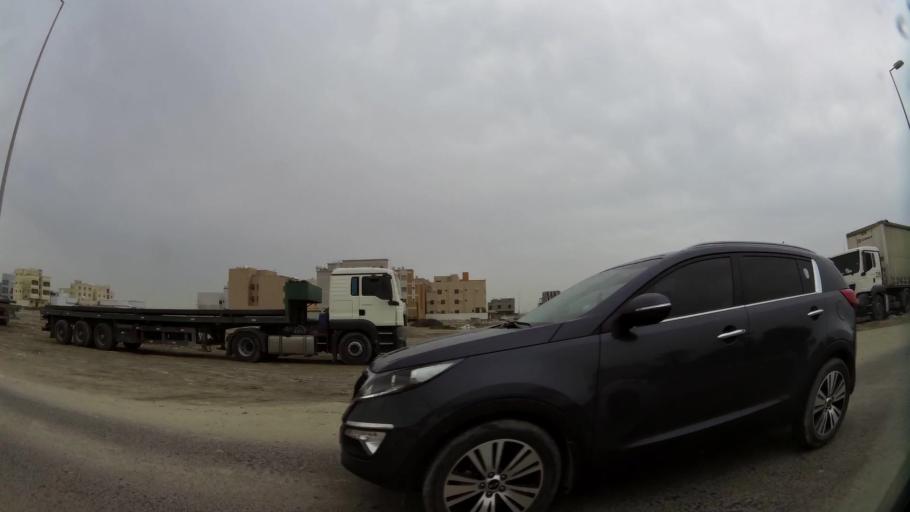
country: BH
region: Northern
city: Madinat `Isa
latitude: 26.1816
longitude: 50.5228
